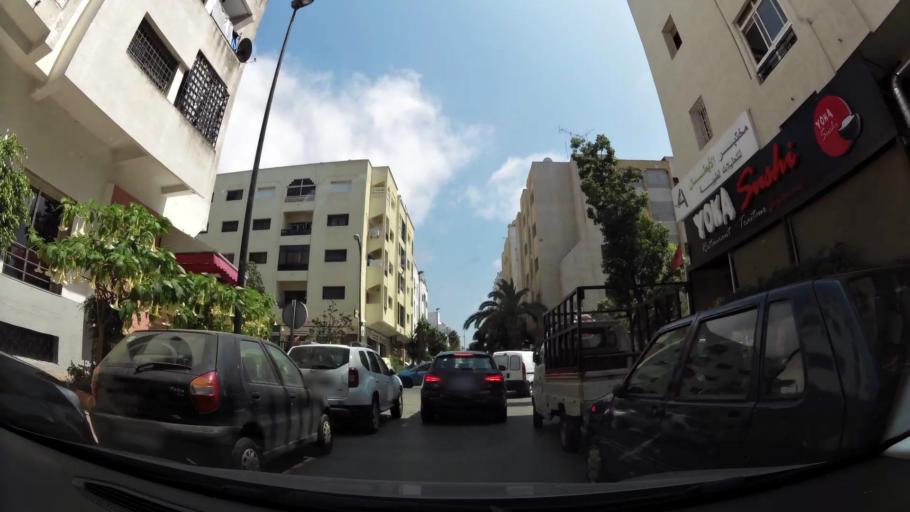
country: MA
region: Rabat-Sale-Zemmour-Zaer
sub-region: Rabat
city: Rabat
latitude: 34.0010
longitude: -6.8495
